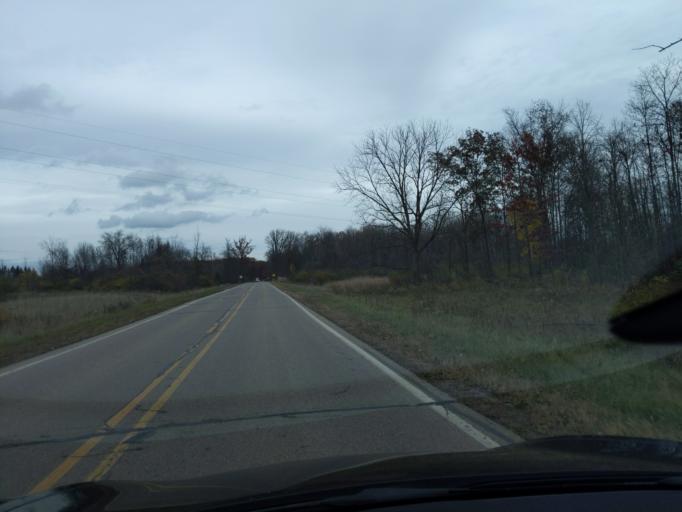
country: US
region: Michigan
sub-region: Ingham County
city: Lansing
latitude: 42.7767
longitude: -84.5378
